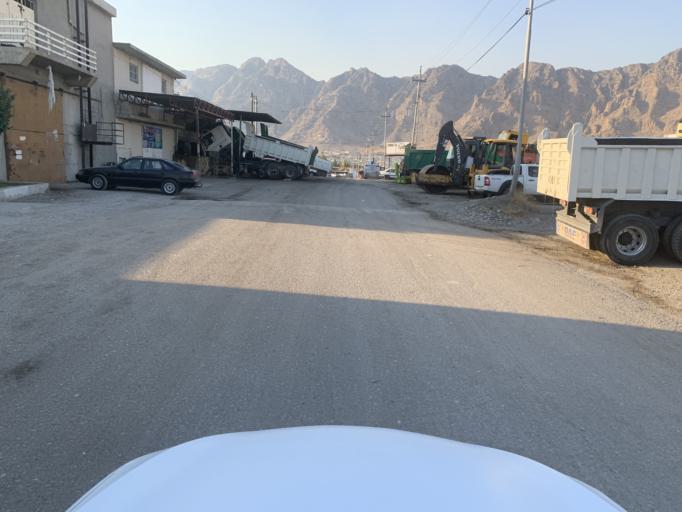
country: IQ
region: As Sulaymaniyah
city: Raniye
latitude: 36.2450
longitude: 44.8887
